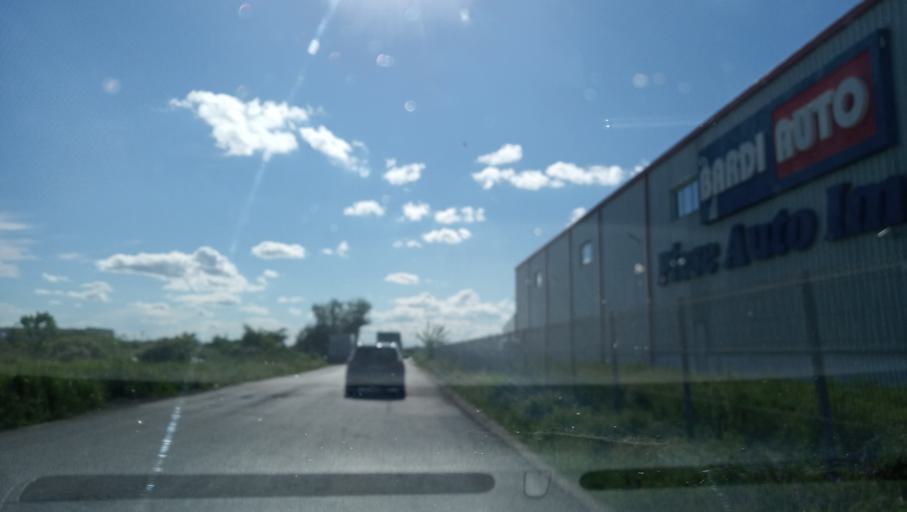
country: RO
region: Ilfov
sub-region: Comuna Chiajna
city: Chiajna
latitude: 44.4421
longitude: 25.9599
